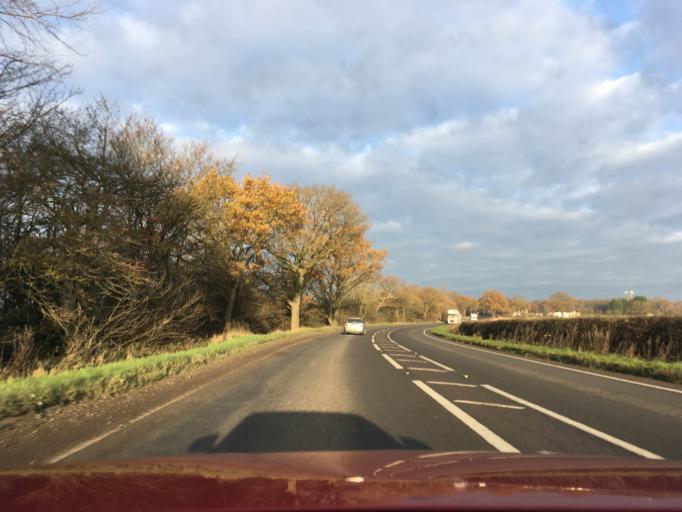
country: GB
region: England
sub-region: City and Borough of Birmingham
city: Sutton Coldfield
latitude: 52.5815
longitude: -1.7777
